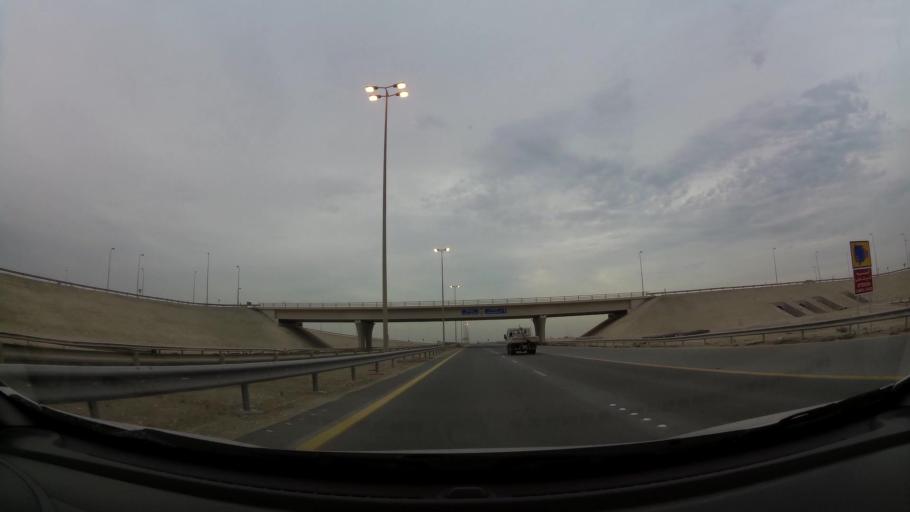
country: BH
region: Northern
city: Ar Rifa'
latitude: 26.0471
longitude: 50.6075
